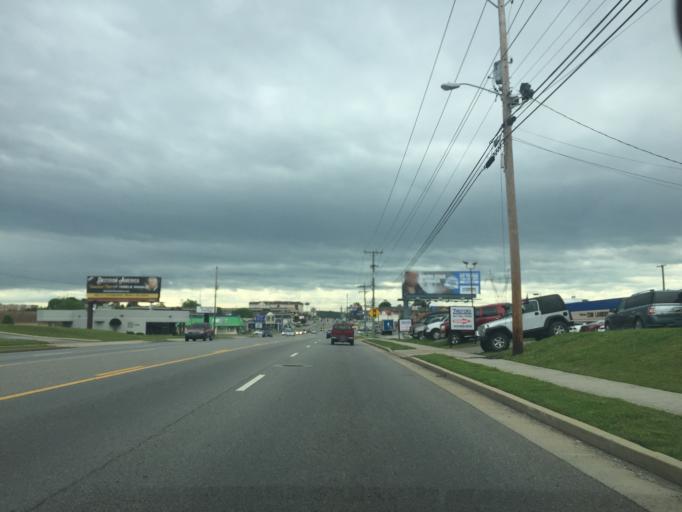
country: US
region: Tennessee
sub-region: Hamilton County
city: East Brainerd
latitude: 35.0460
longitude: -85.1655
